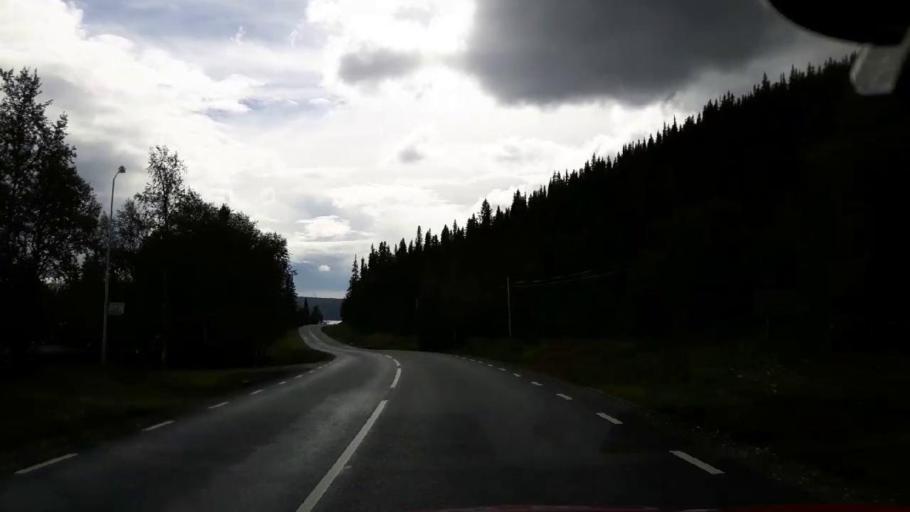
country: NO
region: Nord-Trondelag
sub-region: Royrvik
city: Royrvik
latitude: 64.8334
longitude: 14.0770
